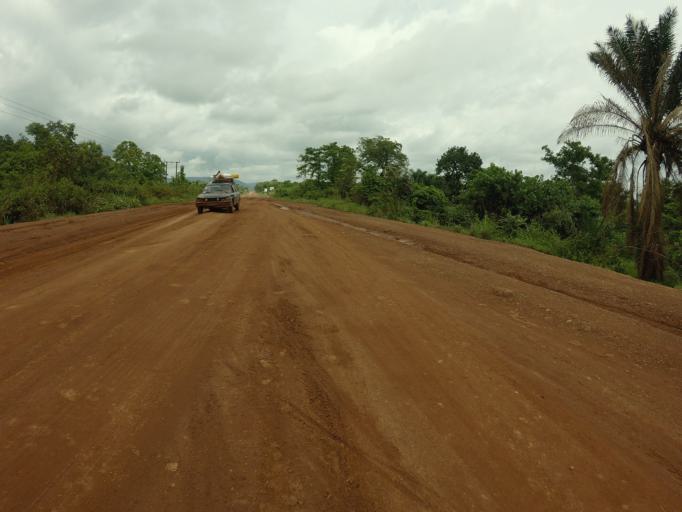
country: GH
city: Kpandae
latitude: 8.2788
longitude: 0.5075
